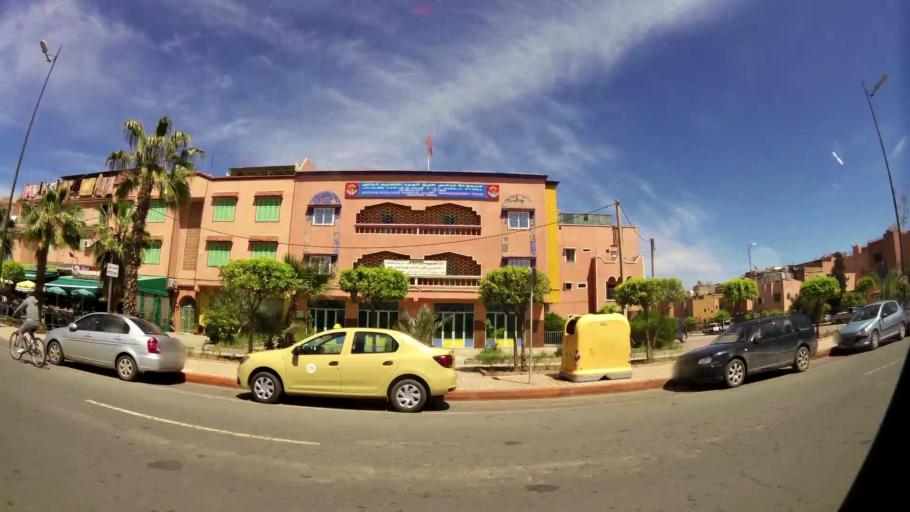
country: MA
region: Marrakech-Tensift-Al Haouz
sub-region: Marrakech
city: Marrakesh
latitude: 31.6053
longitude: -7.9725
